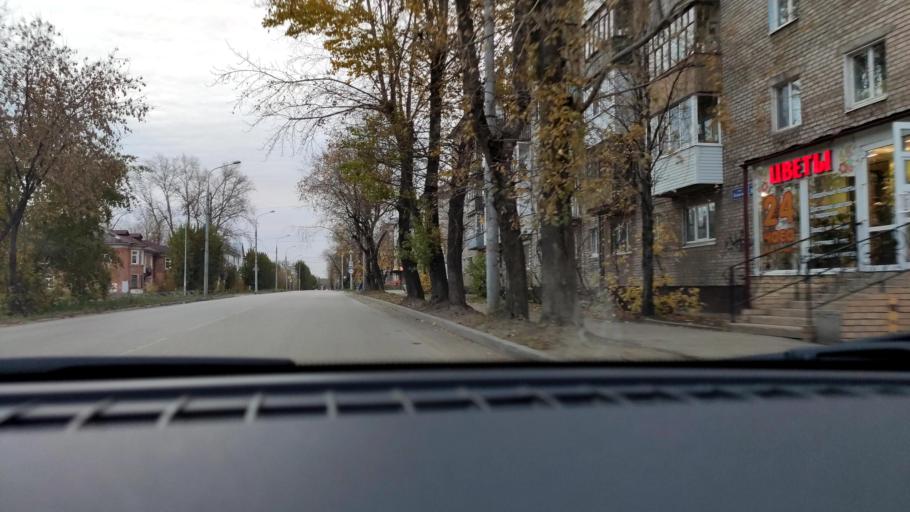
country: RU
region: Perm
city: Perm
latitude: 57.9667
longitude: 56.2253
